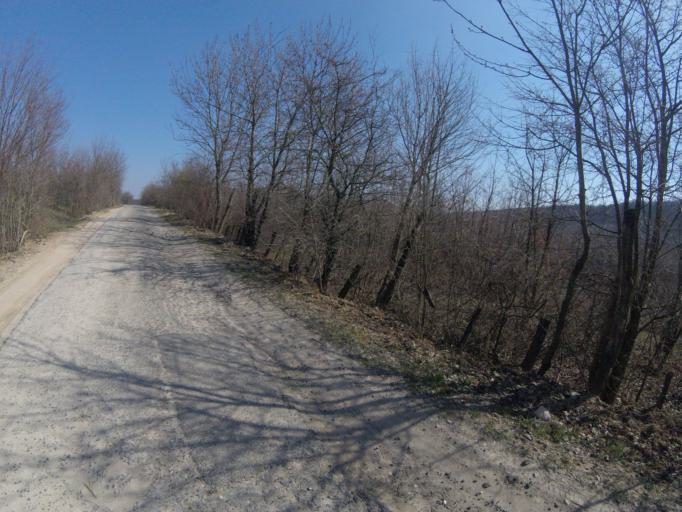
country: HU
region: Pest
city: Budakeszi
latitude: 47.5412
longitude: 18.9303
